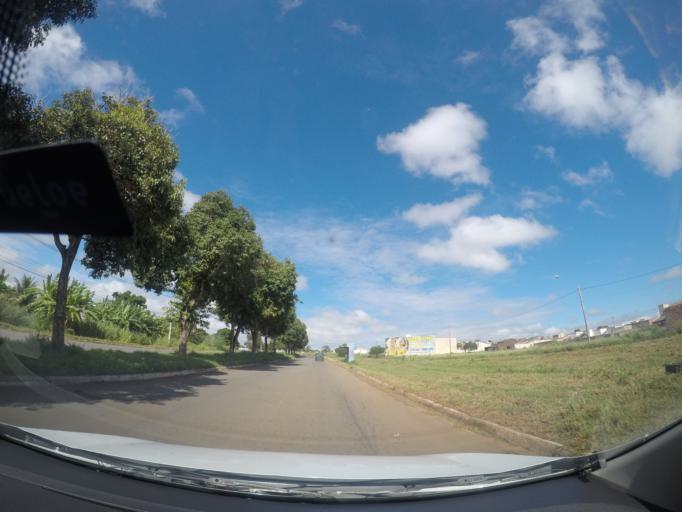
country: BR
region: Goias
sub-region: Goiania
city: Goiania
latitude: -16.6518
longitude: -49.1711
